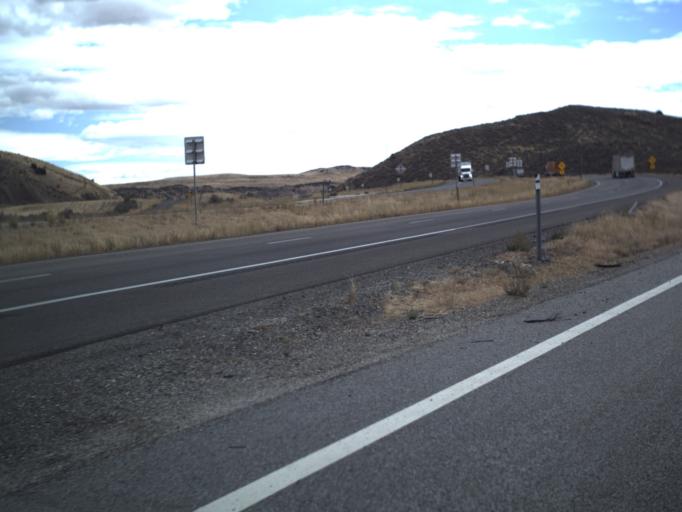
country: US
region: Idaho
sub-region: Oneida County
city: Malad City
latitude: 41.8985
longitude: -112.5783
